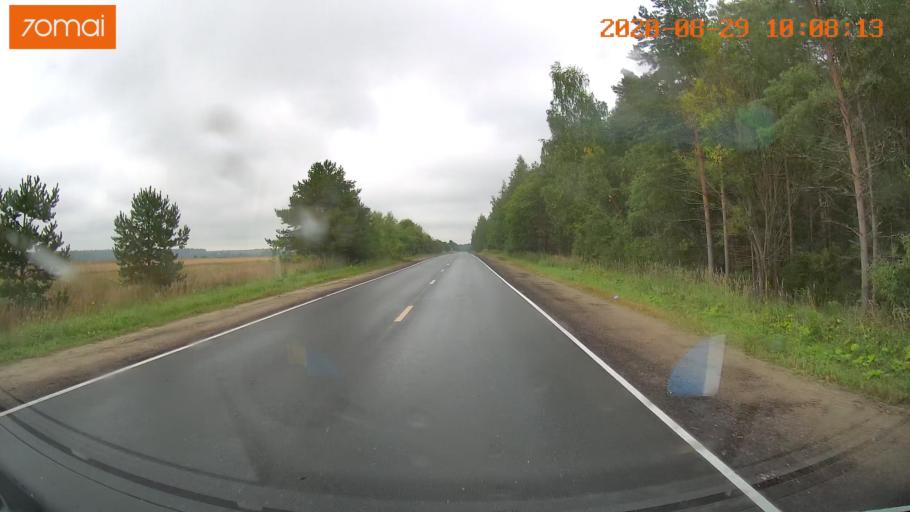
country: RU
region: Ivanovo
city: Kuznechikha
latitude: 57.3767
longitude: 42.5843
